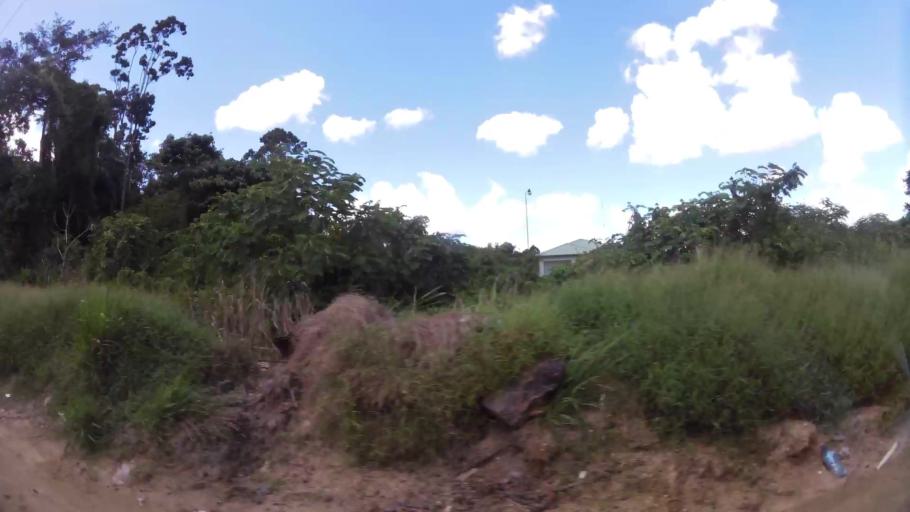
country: SR
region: Paramaribo
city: Paramaribo
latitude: 5.8610
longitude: -55.1544
